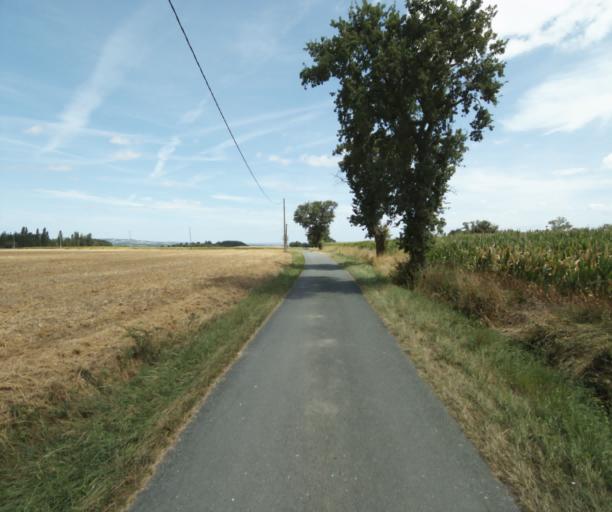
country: FR
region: Midi-Pyrenees
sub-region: Departement du Tarn
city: Soreze
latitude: 43.4807
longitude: 2.0644
